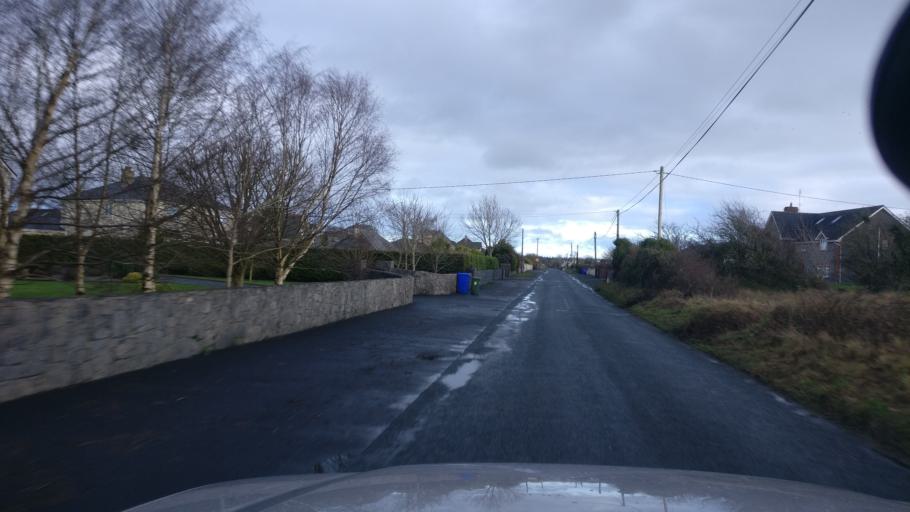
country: IE
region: Connaught
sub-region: County Galway
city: Athenry
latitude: 53.2957
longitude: -8.6871
